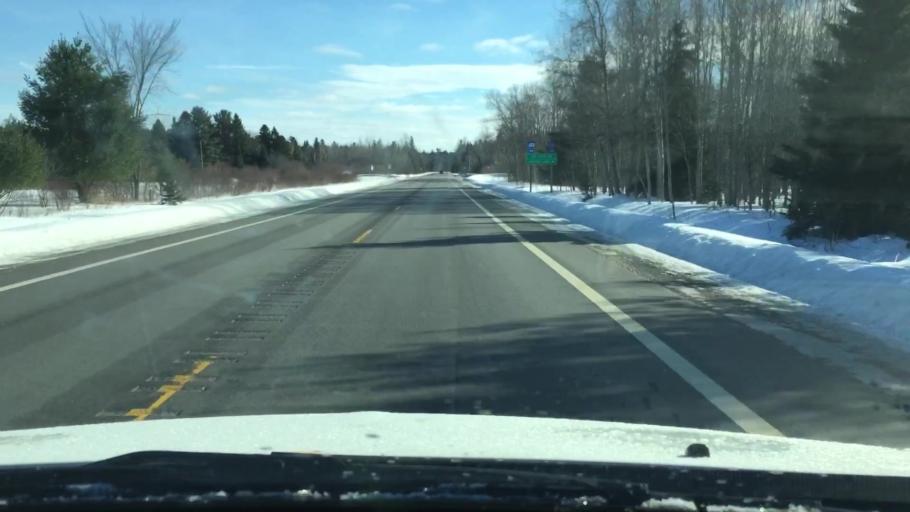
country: US
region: Michigan
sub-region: Charlevoix County
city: East Jordan
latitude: 45.0620
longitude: -85.0794
